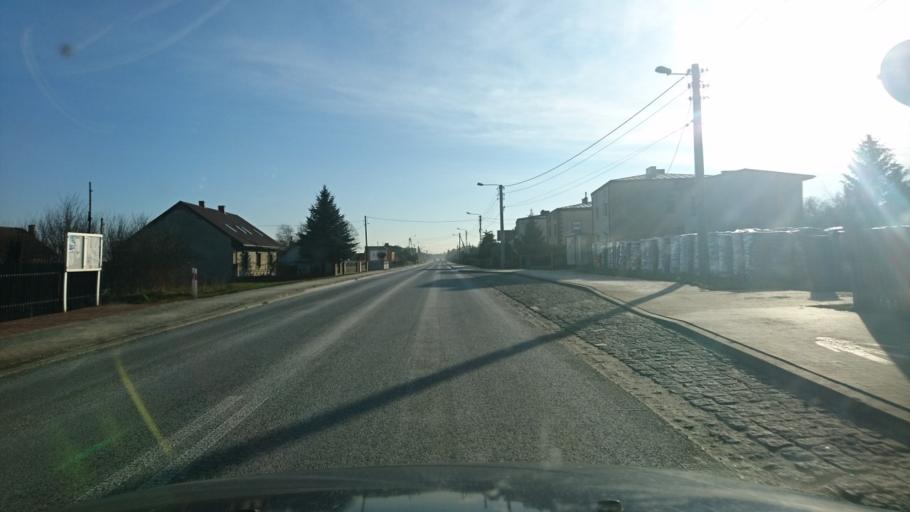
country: PL
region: Silesian Voivodeship
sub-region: Powiat klobucki
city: Starokrzepice
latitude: 51.0149
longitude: 18.6545
